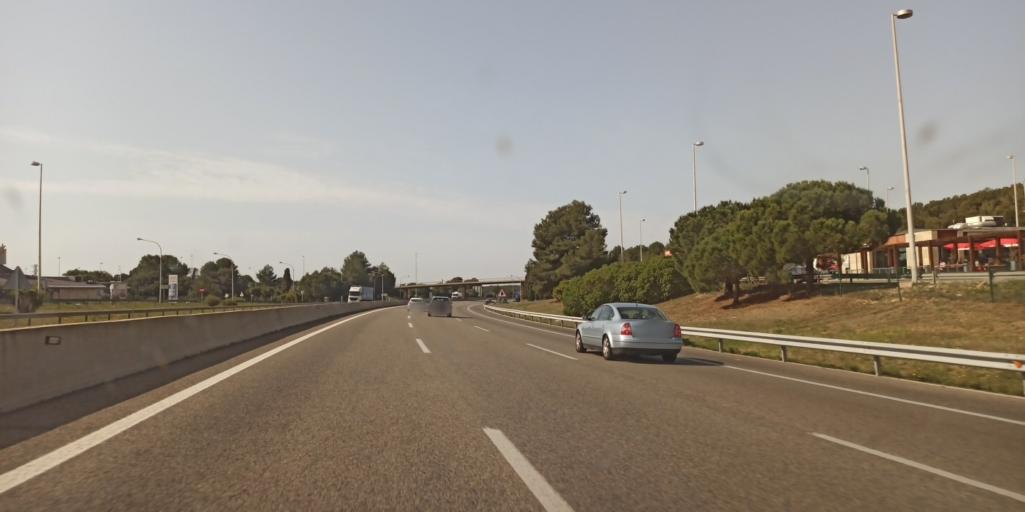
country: ES
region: Catalonia
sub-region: Provincia de Tarragona
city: Altafulla
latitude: 41.1416
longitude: 1.3466
